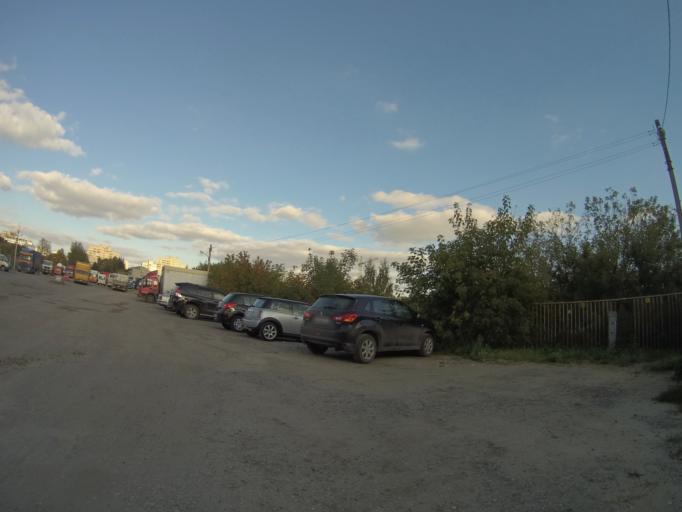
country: RU
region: Vladimir
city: Vladimir
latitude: 56.1139
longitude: 40.3362
